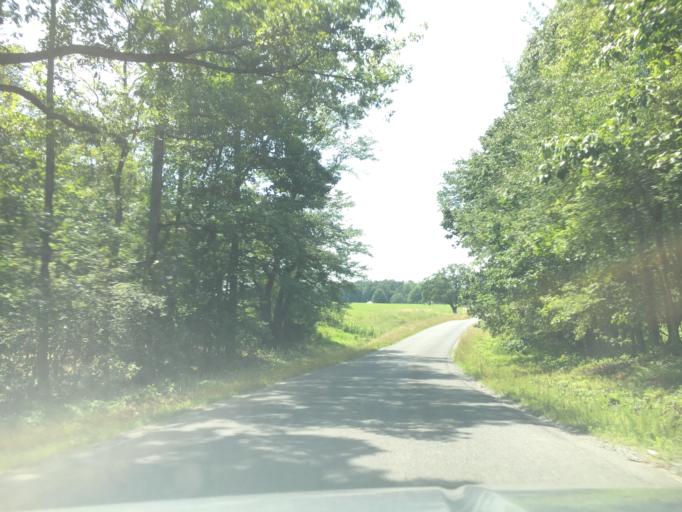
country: US
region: Virginia
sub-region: Pittsylvania County
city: Gretna
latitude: 36.9098
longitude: -79.4158
